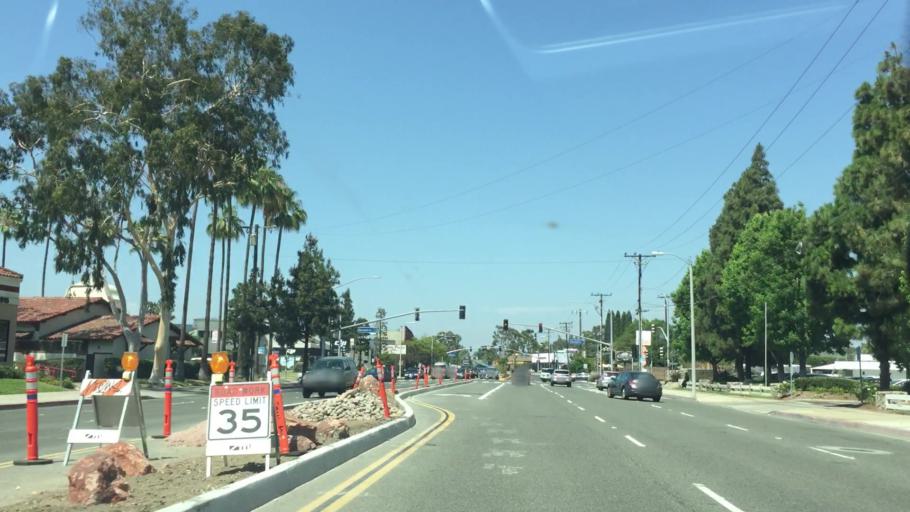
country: US
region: California
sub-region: Orange County
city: Costa Mesa
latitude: 33.6762
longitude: -117.8880
